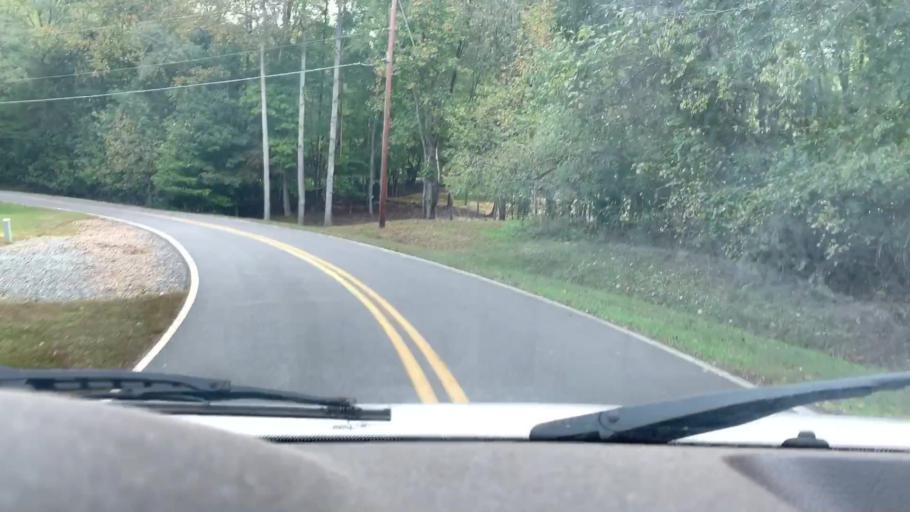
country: US
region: North Carolina
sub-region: Catawba County
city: Lake Norman of Catawba
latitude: 35.5728
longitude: -80.9481
